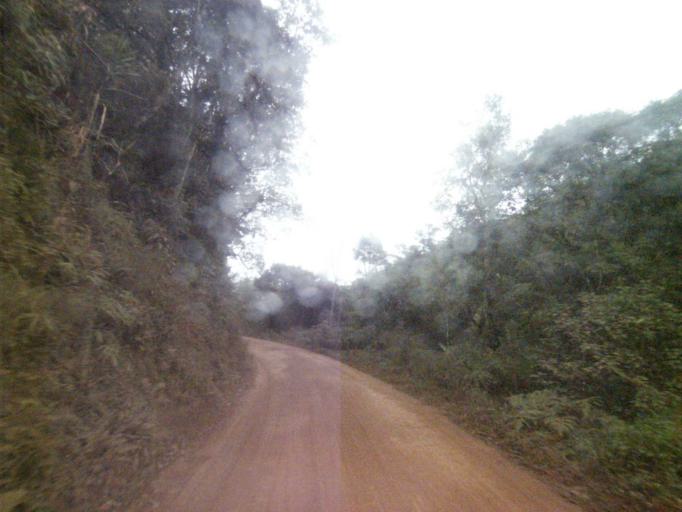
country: BR
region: Santa Catarina
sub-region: Anitapolis
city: Anitapolis
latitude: -27.8941
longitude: -49.1294
